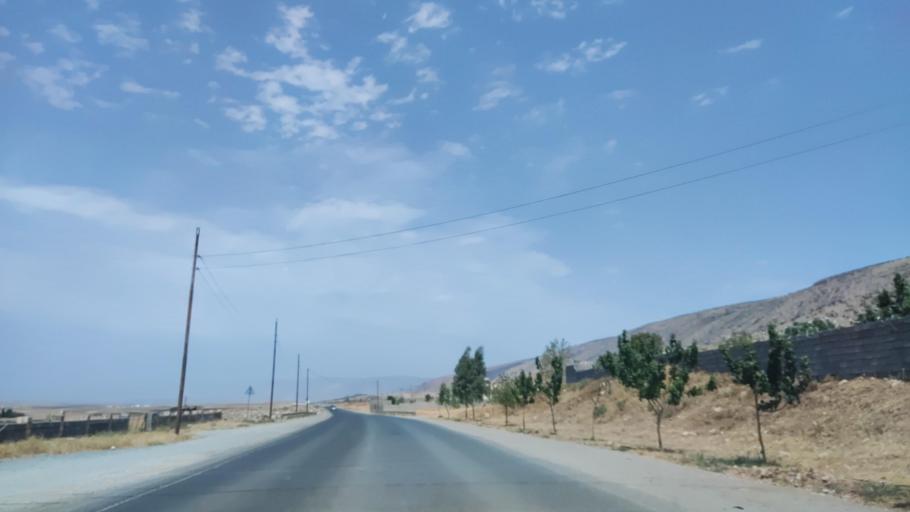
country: IQ
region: Arbil
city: Shaqlawah
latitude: 36.4928
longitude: 44.3945
